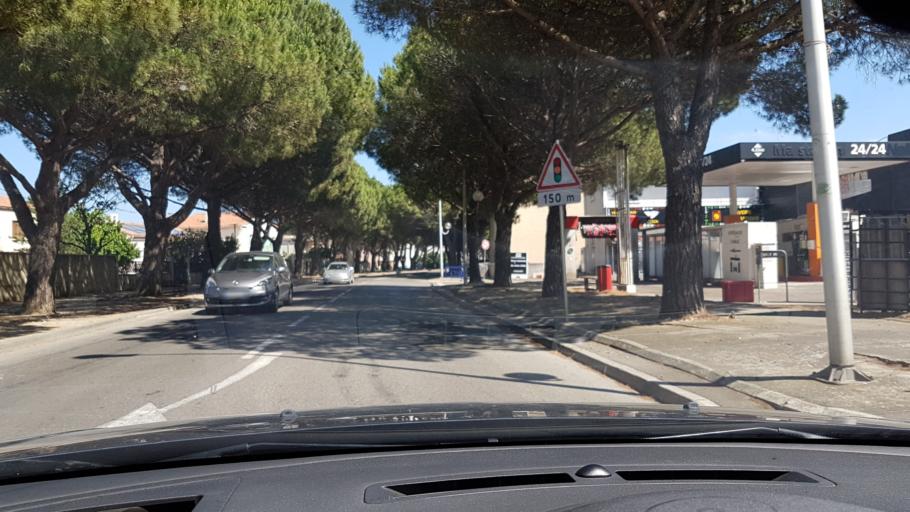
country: FR
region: Provence-Alpes-Cote d'Azur
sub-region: Departement des Bouches-du-Rhone
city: Port-Saint-Louis-du-Rhone
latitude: 43.3992
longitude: 4.7919
